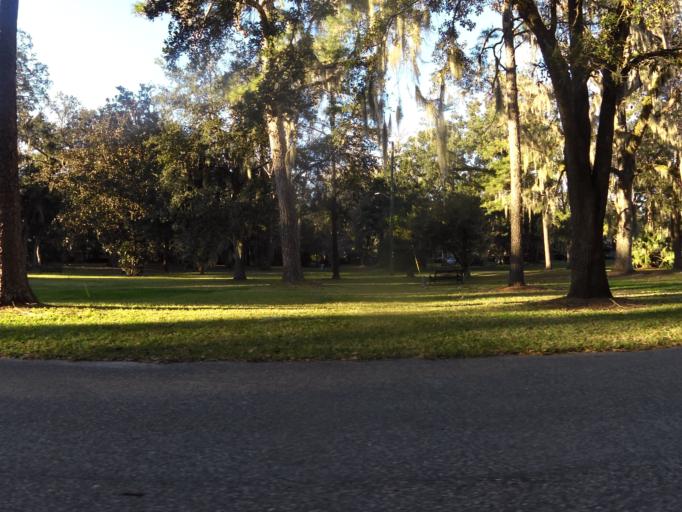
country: US
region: Florida
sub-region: Duval County
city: Jacksonville
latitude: 30.2710
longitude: -81.7052
